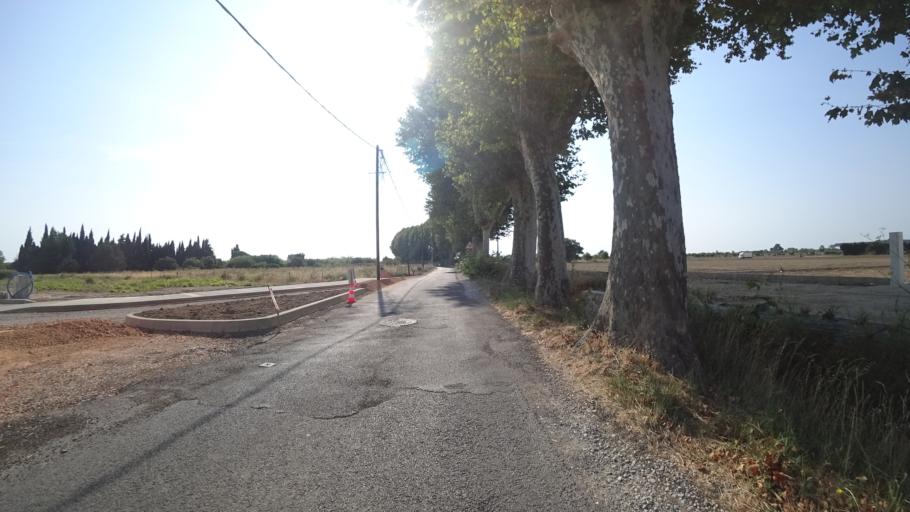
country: FR
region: Languedoc-Roussillon
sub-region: Departement des Pyrenees-Orientales
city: Claira
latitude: 42.7597
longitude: 2.9620
